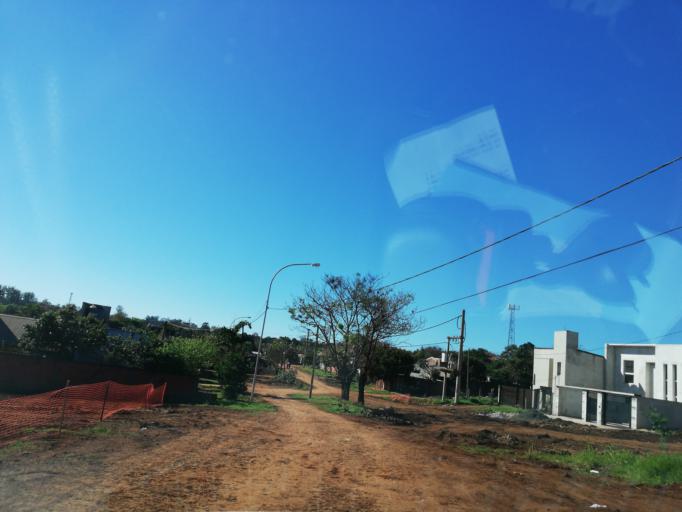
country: AR
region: Misiones
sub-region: Departamento de Capital
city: Posadas
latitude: -27.3932
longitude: -55.9408
